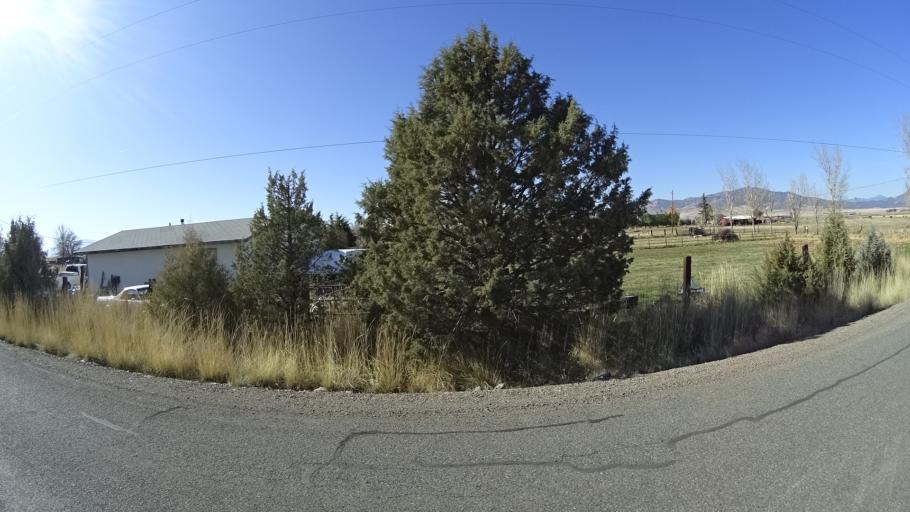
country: US
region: California
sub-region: Siskiyou County
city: Montague
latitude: 41.7589
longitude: -122.4571
